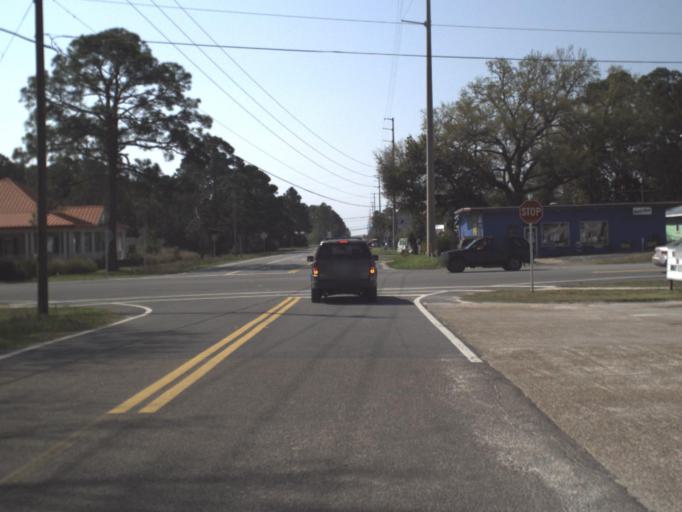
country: US
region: Florida
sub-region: Franklin County
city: Eastpoint
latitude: 29.7366
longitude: -84.8881
